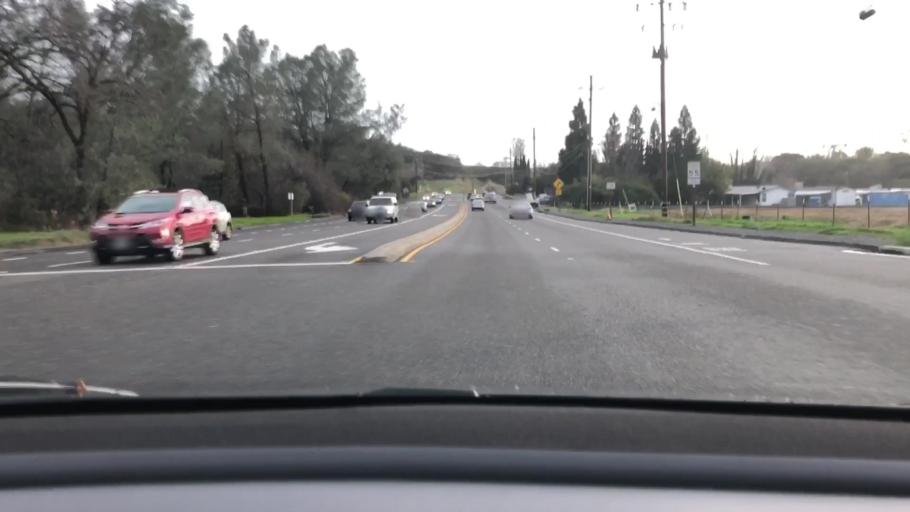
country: US
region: California
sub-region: Placer County
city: Granite Bay
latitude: 38.7360
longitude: -121.1706
